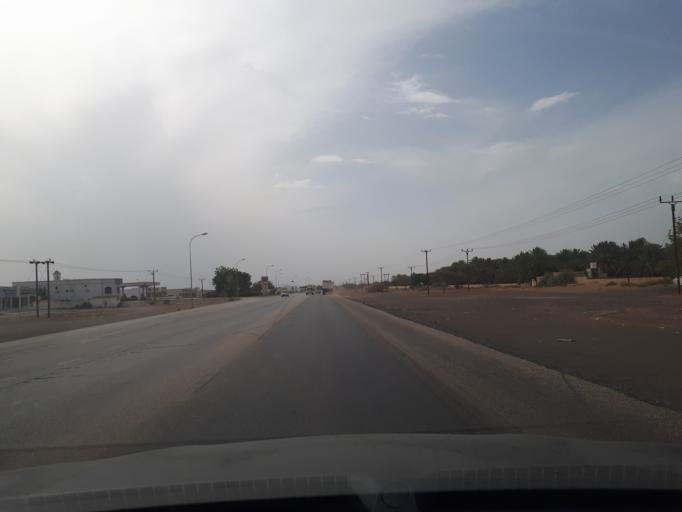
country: OM
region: Ash Sharqiyah
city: Badiyah
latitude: 22.4926
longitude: 58.7602
